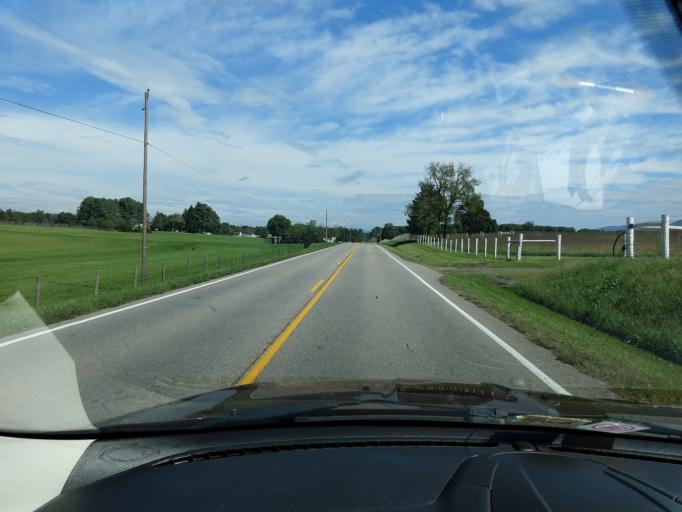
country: US
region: Virginia
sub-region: Augusta County
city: Crimora
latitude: 38.1954
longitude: -78.8378
